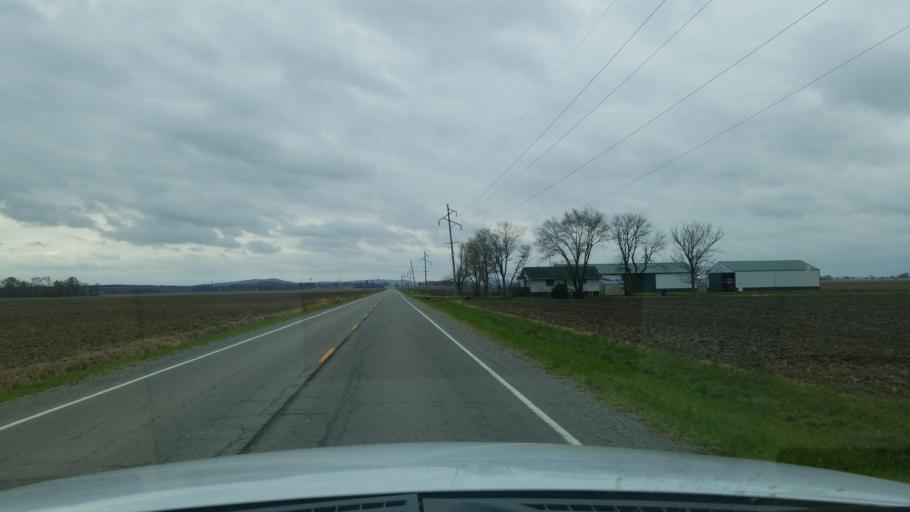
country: US
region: Illinois
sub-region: Saline County
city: Eldorado
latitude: 37.7843
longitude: -88.4382
